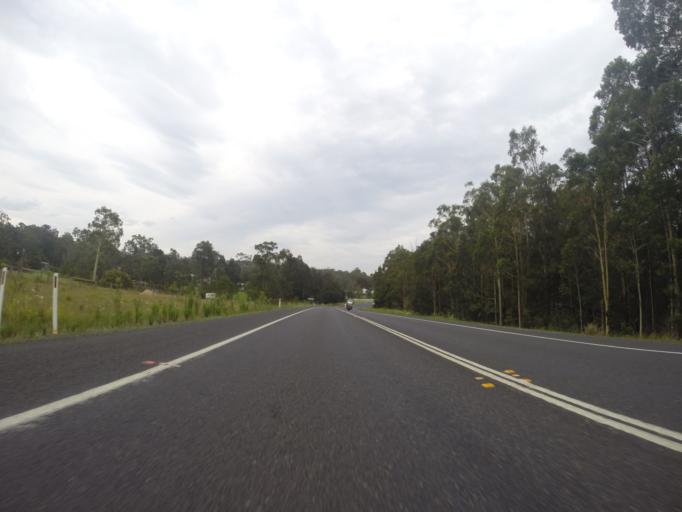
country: AU
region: New South Wales
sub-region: Eurobodalla
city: Batemans Bay
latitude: -35.6841
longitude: 150.2028
